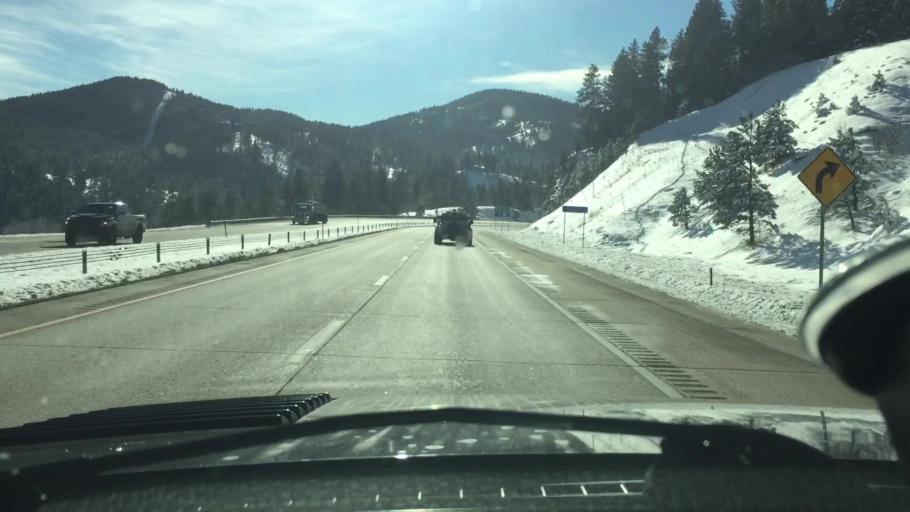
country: US
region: Colorado
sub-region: Jefferson County
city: Indian Hills
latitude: 39.5964
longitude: -105.2243
